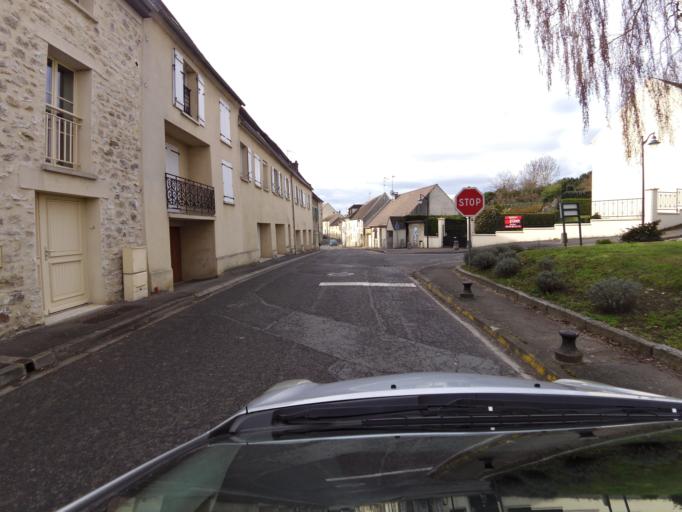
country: FR
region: Picardie
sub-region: Departement de l'Oise
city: Ver-sur-Launette
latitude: 49.1040
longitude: 2.6858
